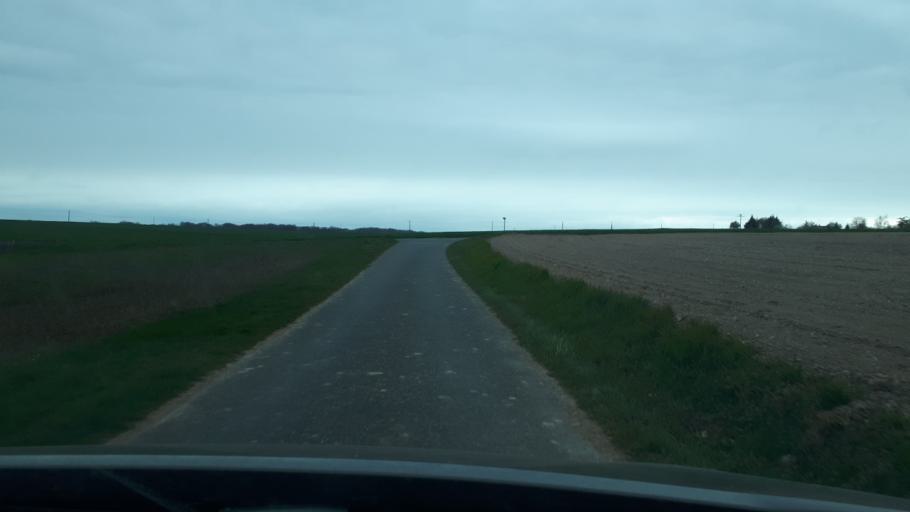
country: FR
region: Centre
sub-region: Departement du Loir-et-Cher
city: Lunay
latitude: 47.7520
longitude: 0.9514
